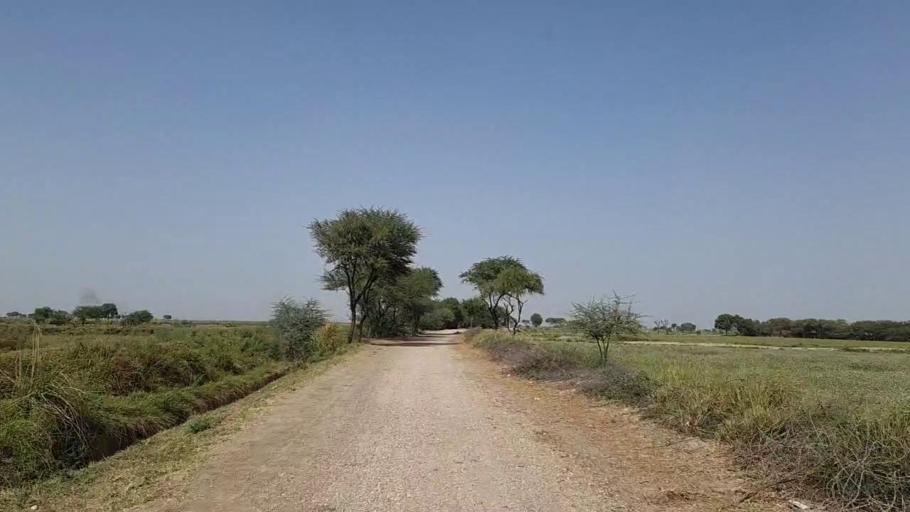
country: PK
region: Sindh
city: Jati
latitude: 24.3460
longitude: 68.3063
